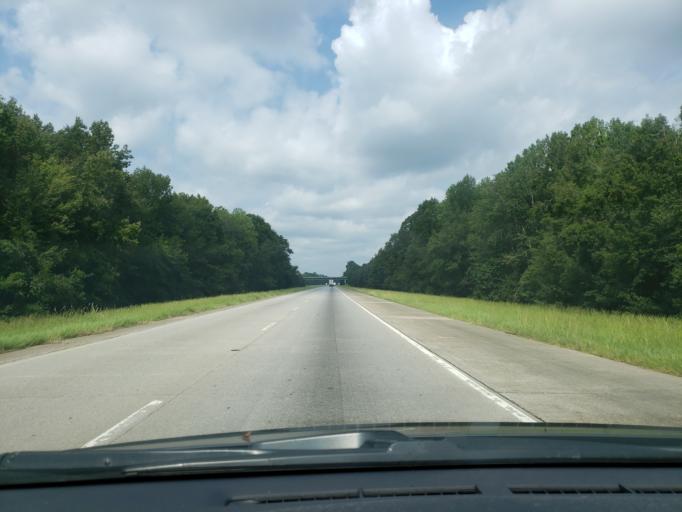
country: US
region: Georgia
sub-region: Treutlen County
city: Soperton
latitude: 32.4235
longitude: -82.4277
